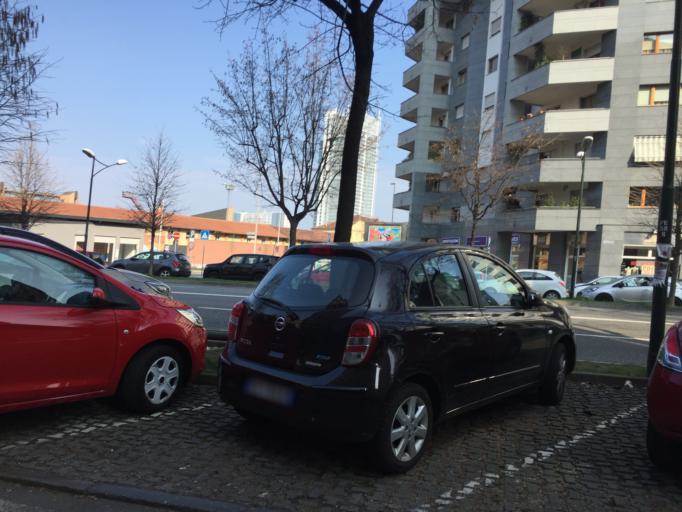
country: IT
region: Piedmont
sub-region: Provincia di Torino
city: Turin
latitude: 45.0686
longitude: 7.6551
